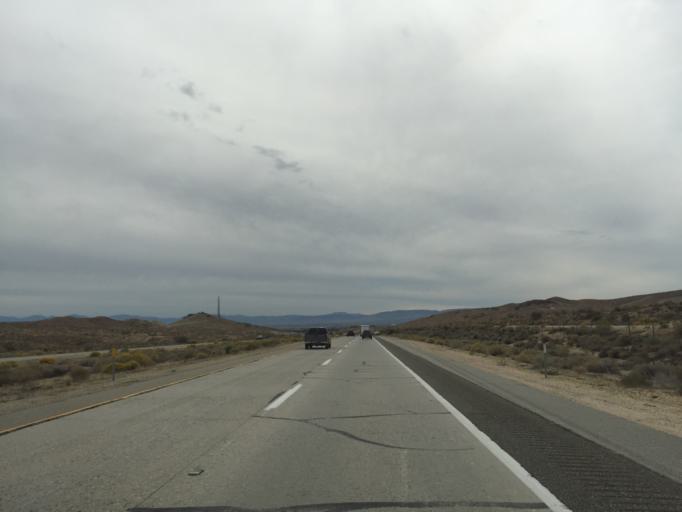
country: US
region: California
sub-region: Kern County
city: Rosamond
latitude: 34.8951
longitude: -118.1657
